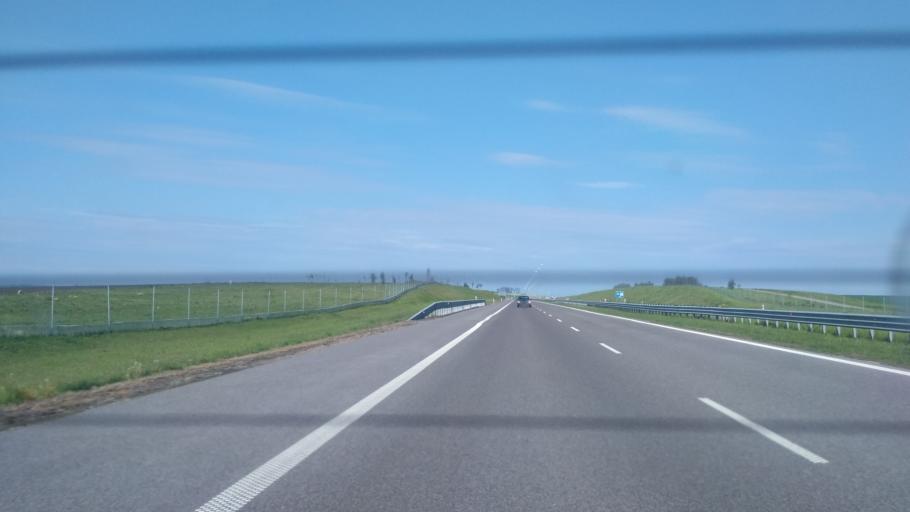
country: PL
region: Subcarpathian Voivodeship
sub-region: Powiat przemyski
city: Orly
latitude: 49.9157
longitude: 22.7724
